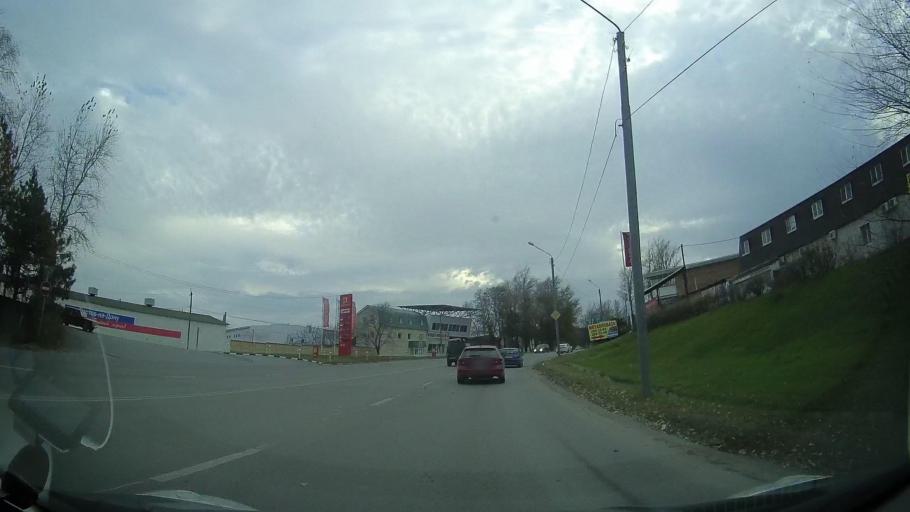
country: RU
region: Rostov
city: Aksay
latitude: 47.2447
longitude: 39.8418
